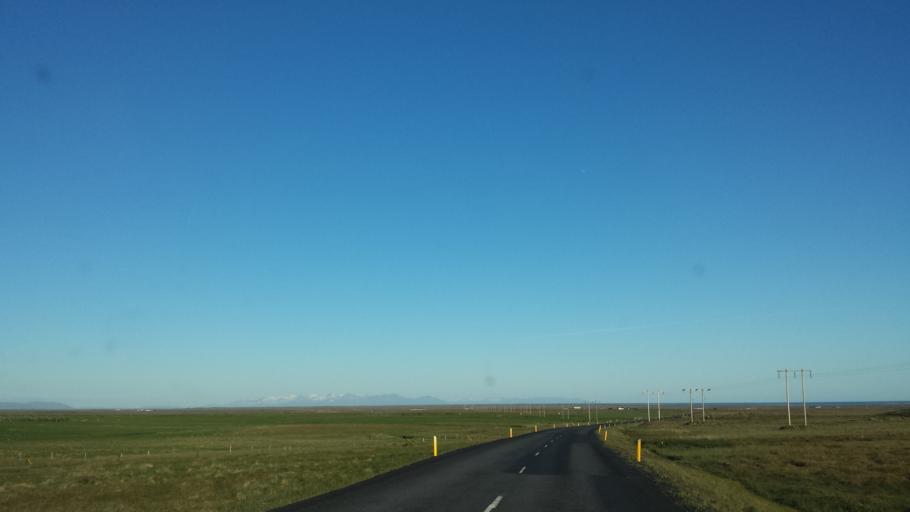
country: IS
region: West
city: Stykkisholmur
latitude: 64.8689
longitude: -22.7607
